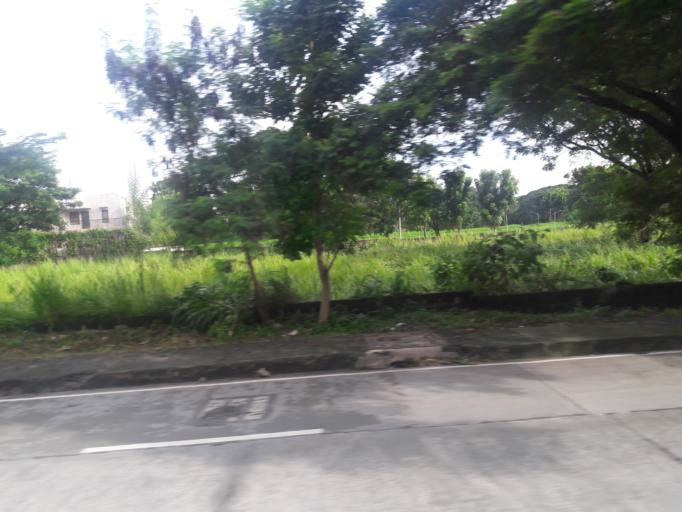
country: PH
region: Calabarzon
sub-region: Province of Cavite
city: Carmona
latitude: 14.3135
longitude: 121.0483
